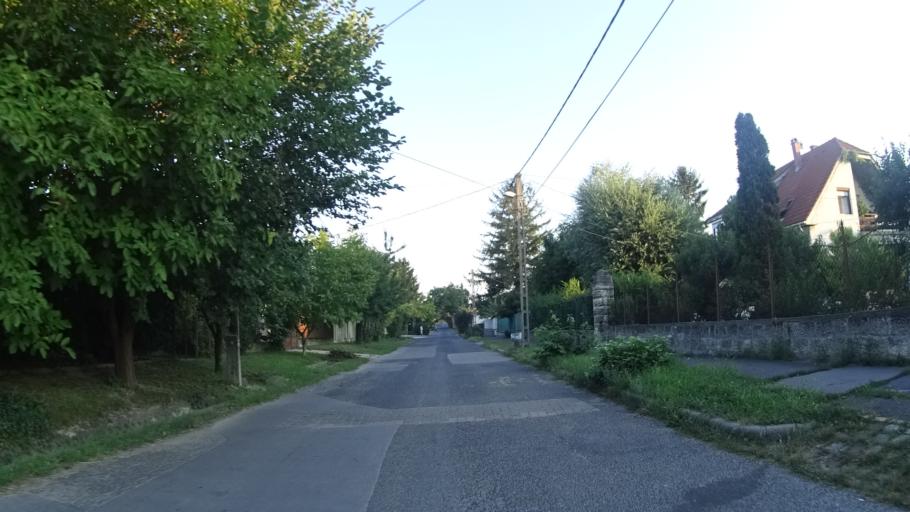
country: HU
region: Pest
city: Halasztelek
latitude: 47.3944
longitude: 19.0056
